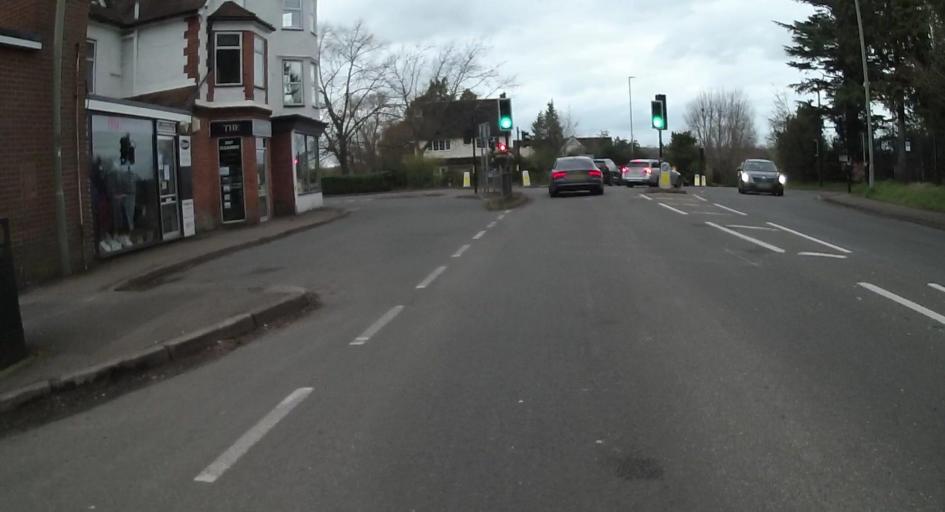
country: GB
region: England
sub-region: Surrey
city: Farnham
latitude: 51.2036
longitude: -0.7937
